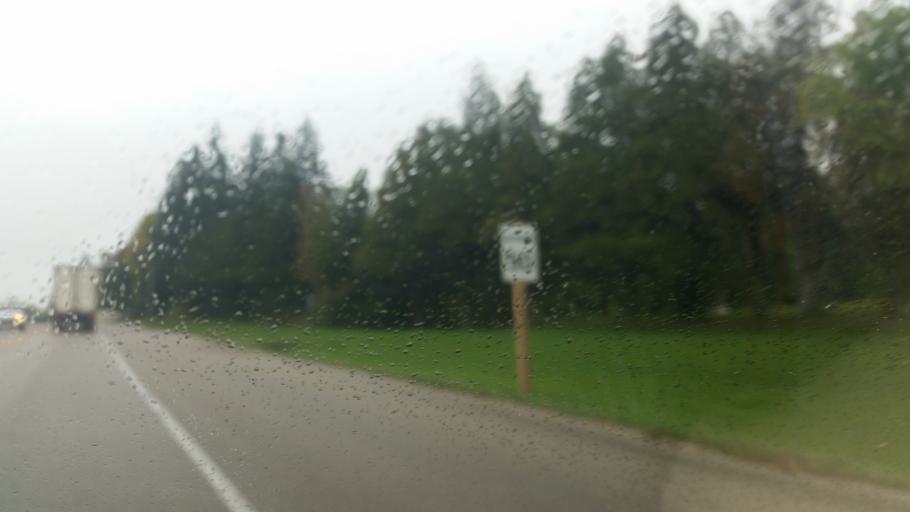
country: CA
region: Ontario
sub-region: Wellington County
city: Guelph
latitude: 43.6833
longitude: -80.4383
